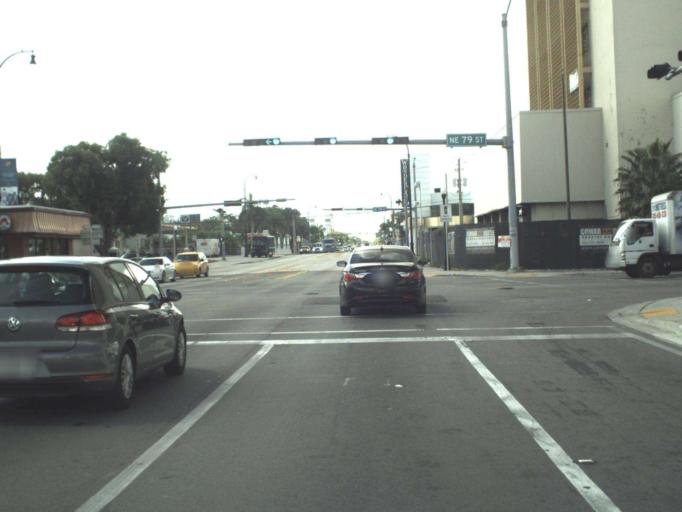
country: US
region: Florida
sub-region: Miami-Dade County
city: El Portal
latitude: 25.8481
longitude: -80.1847
